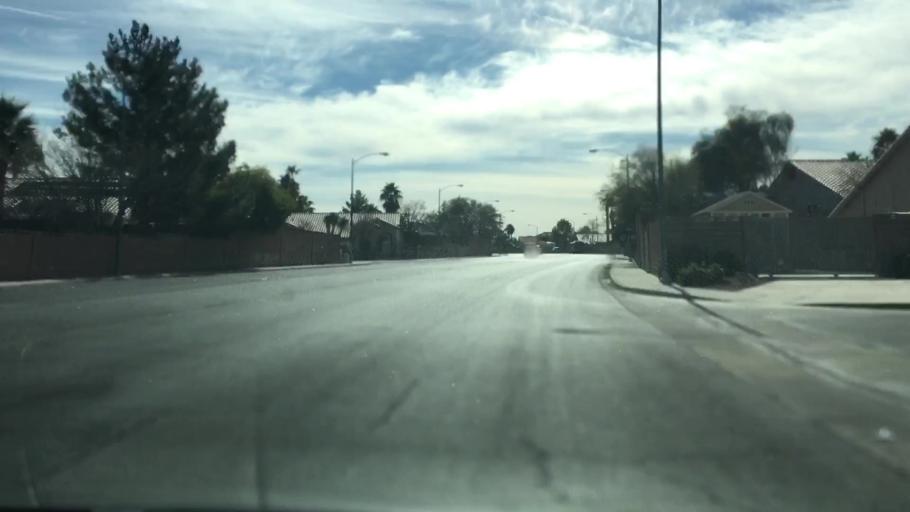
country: US
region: Nevada
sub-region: Clark County
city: Whitney
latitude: 36.0413
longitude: -115.1274
